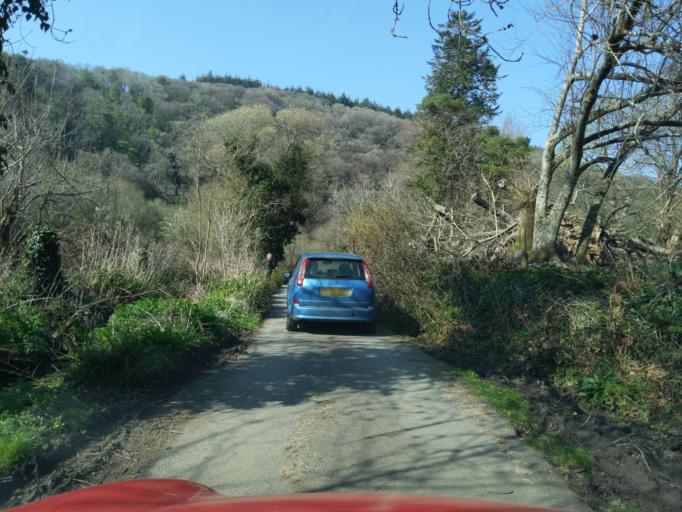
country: GB
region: England
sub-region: Devon
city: Bere Alston
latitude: 50.4615
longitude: -4.1546
